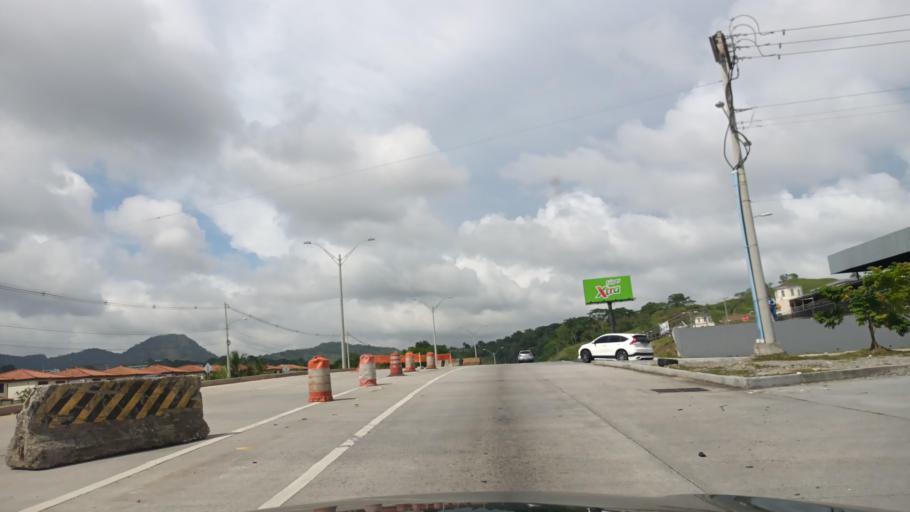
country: PA
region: Panama
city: Las Cumbres
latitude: 9.1019
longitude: -79.5204
